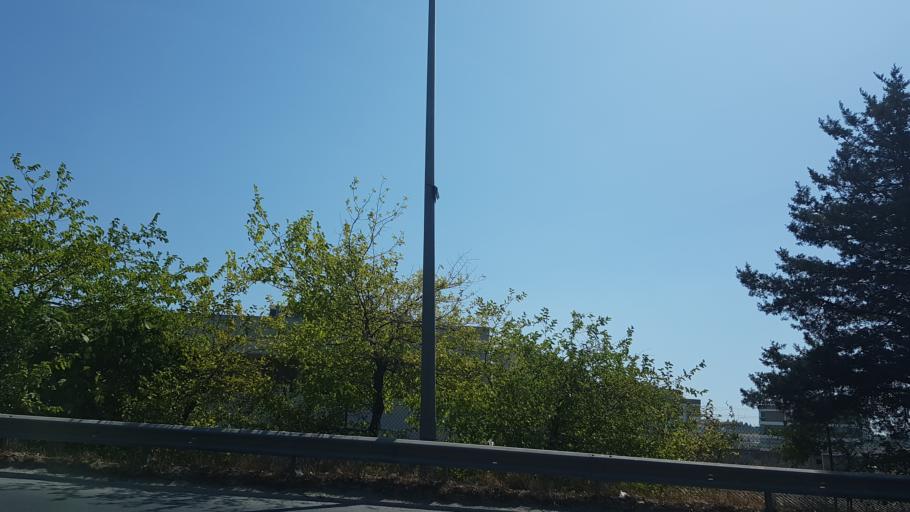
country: TR
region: Izmir
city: Gaziemir
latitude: 38.3413
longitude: 27.1335
